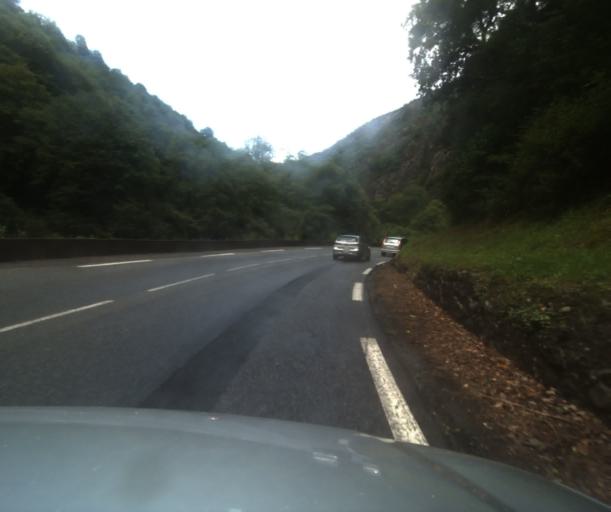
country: FR
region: Midi-Pyrenees
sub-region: Departement des Hautes-Pyrenees
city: Pierrefitte-Nestalas
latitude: 42.9402
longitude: -0.0533
